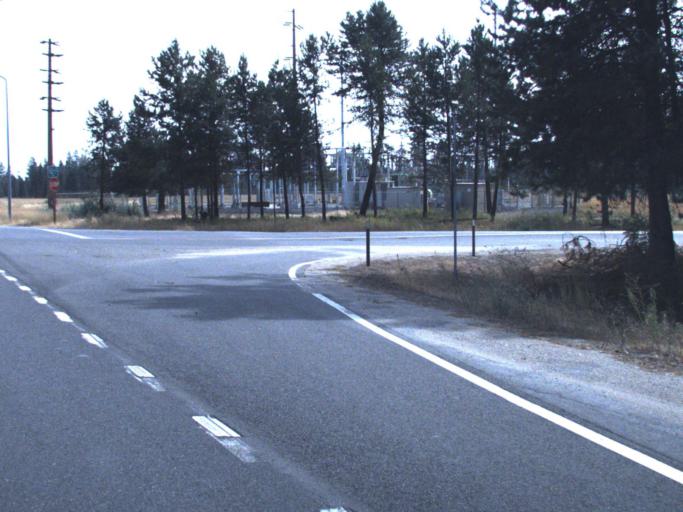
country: US
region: Washington
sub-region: Spokane County
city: Deer Park
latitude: 47.9606
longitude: -117.4967
